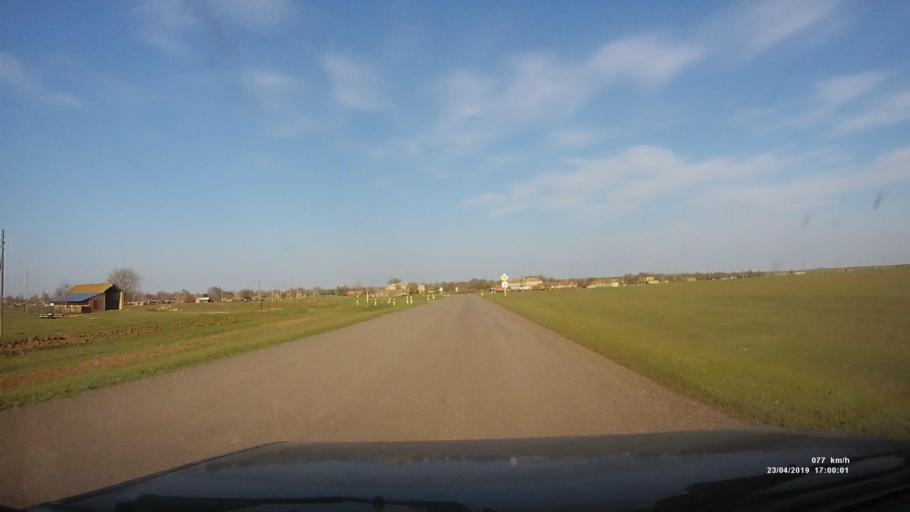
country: RU
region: Kalmykiya
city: Priyutnoye
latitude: 46.3084
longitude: 43.4006
